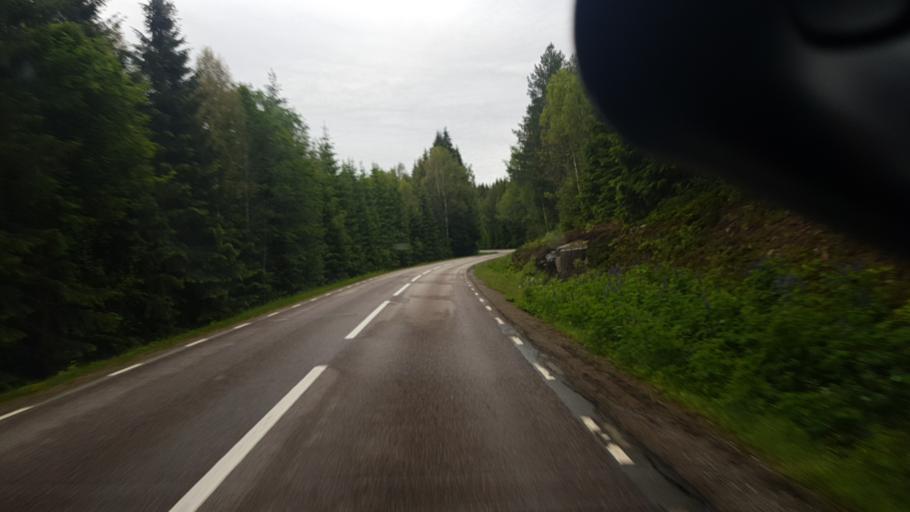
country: SE
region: Vaermland
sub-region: Eda Kommun
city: Amotfors
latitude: 59.6419
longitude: 12.3545
